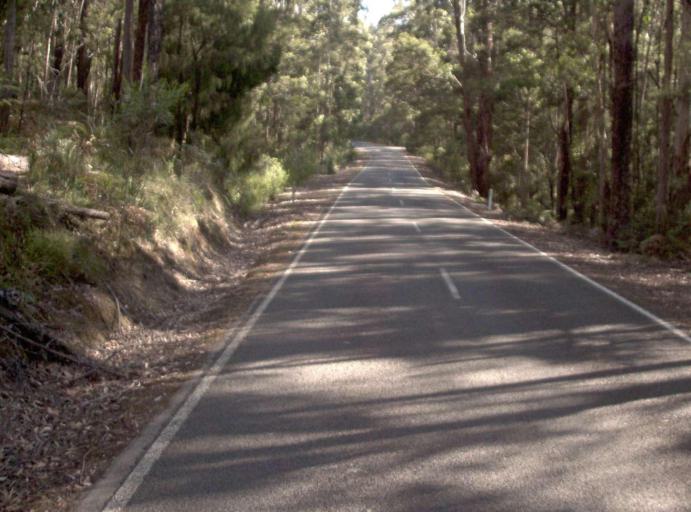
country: AU
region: Victoria
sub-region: East Gippsland
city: Lakes Entrance
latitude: -37.6217
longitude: 148.5114
